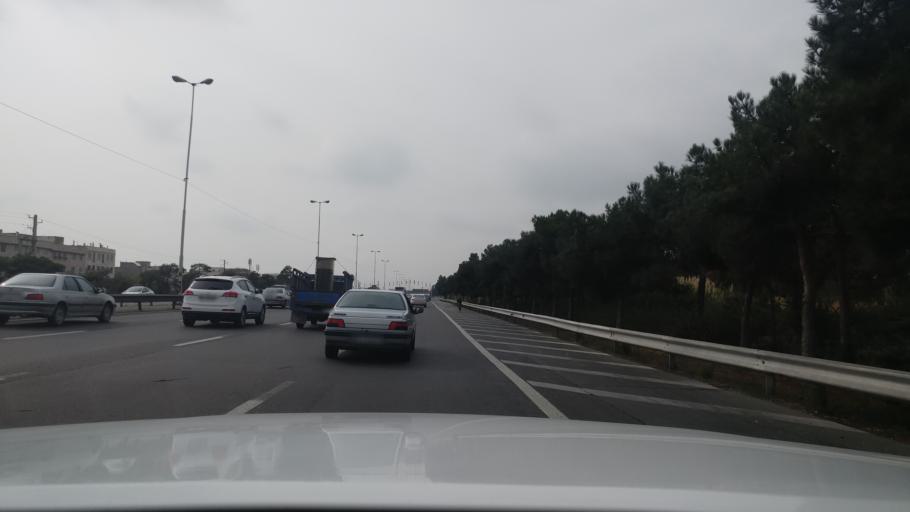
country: IR
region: Tehran
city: Tehran
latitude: 35.7156
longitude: 51.2731
